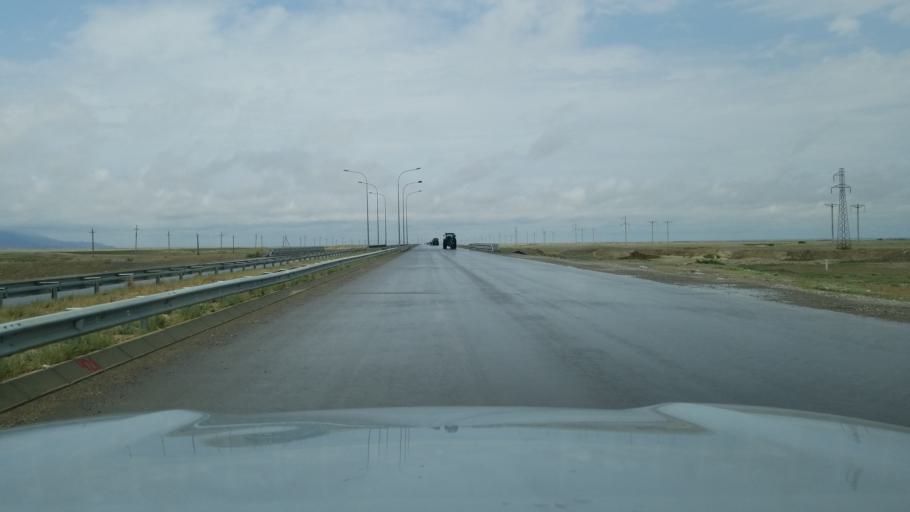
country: TM
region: Balkan
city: Gazanjyk
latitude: 39.1737
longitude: 55.8160
